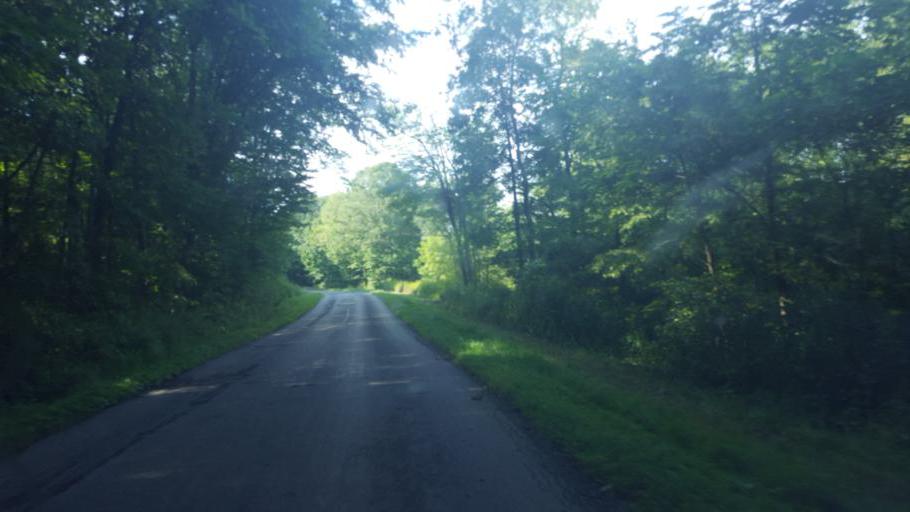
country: US
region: Ohio
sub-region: Knox County
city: Danville
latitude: 40.4767
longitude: -82.3036
